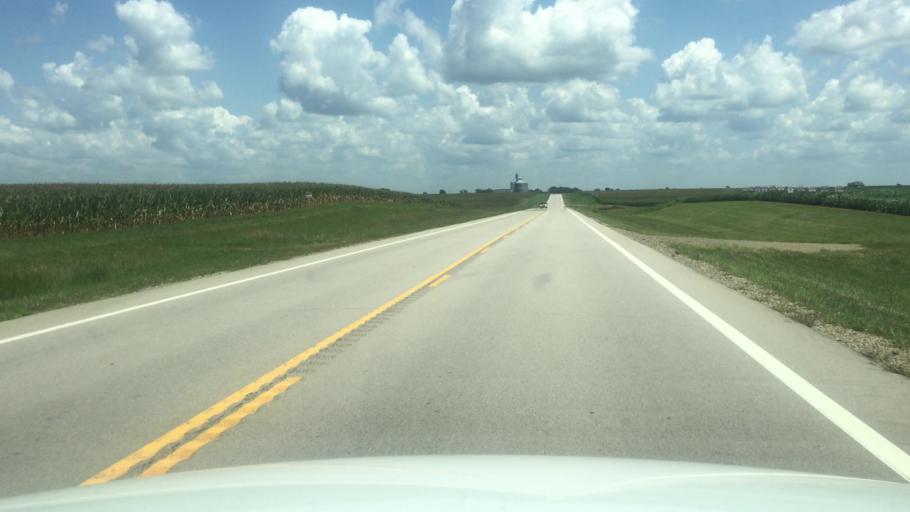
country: US
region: Kansas
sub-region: Brown County
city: Horton
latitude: 39.6602
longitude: -95.4014
